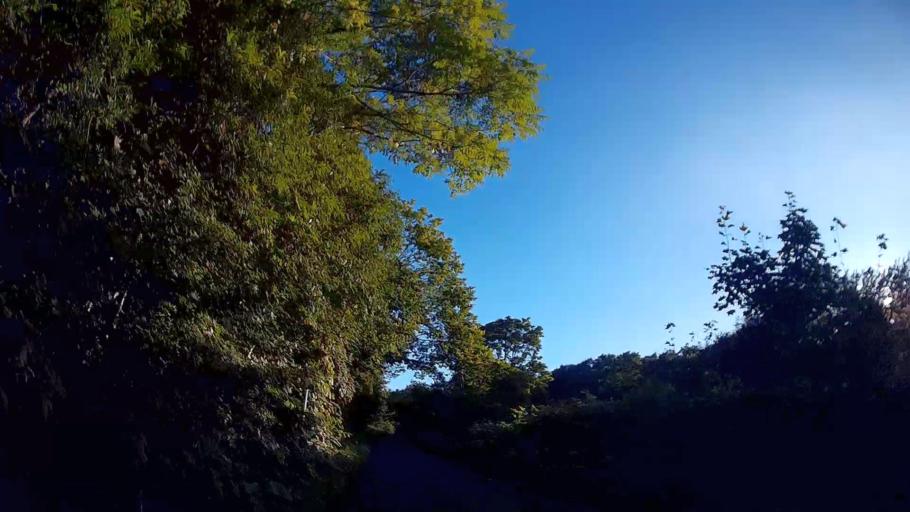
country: JP
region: Hokkaido
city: Iwanai
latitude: 42.6300
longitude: 140.0282
